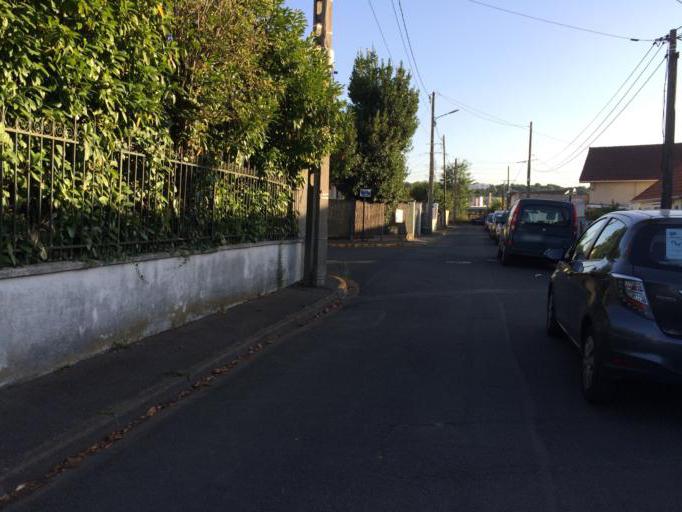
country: FR
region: Ile-de-France
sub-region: Departement de l'Essonne
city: Palaiseau
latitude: 48.7289
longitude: 2.2484
